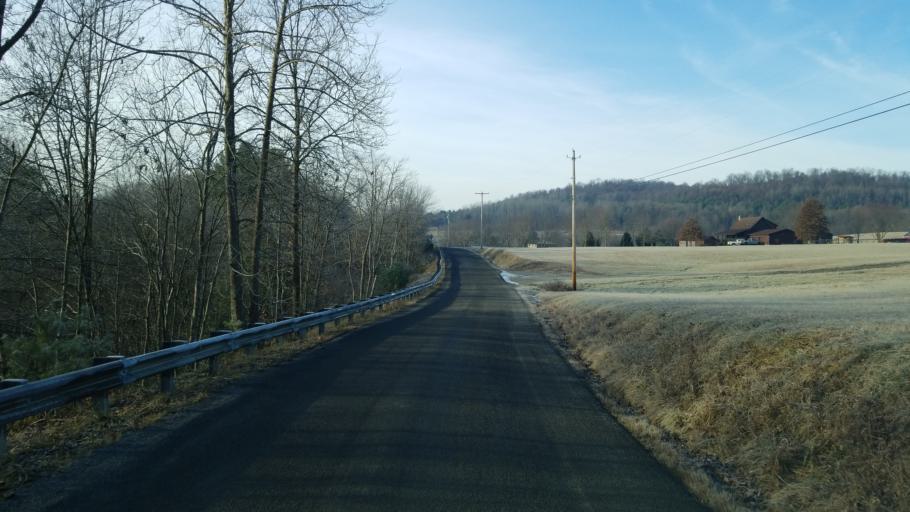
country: US
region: Pennsylvania
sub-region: Jefferson County
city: Brookville
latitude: 40.9545
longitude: -79.2644
